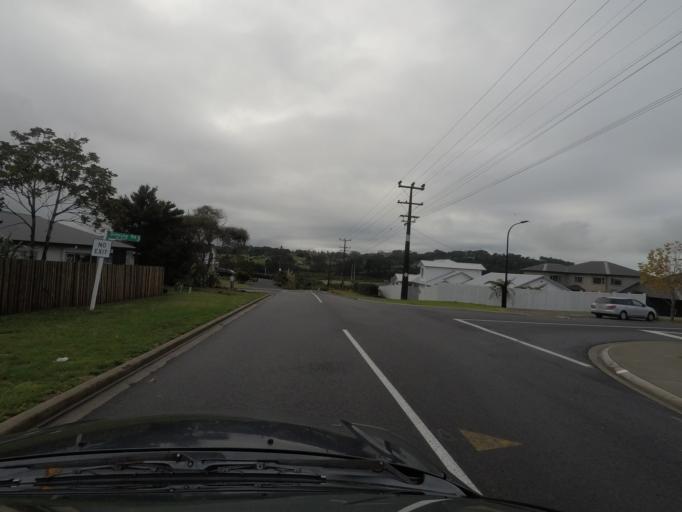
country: NZ
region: Auckland
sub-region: Auckland
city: Rosebank
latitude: -36.7629
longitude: 174.5957
